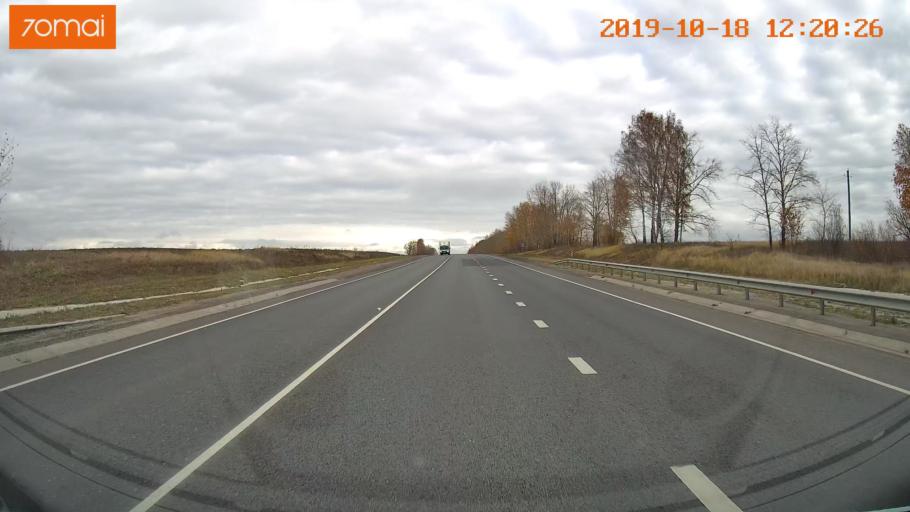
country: RU
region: Rjazan
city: Bagramovo
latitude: 54.4975
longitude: 39.4801
